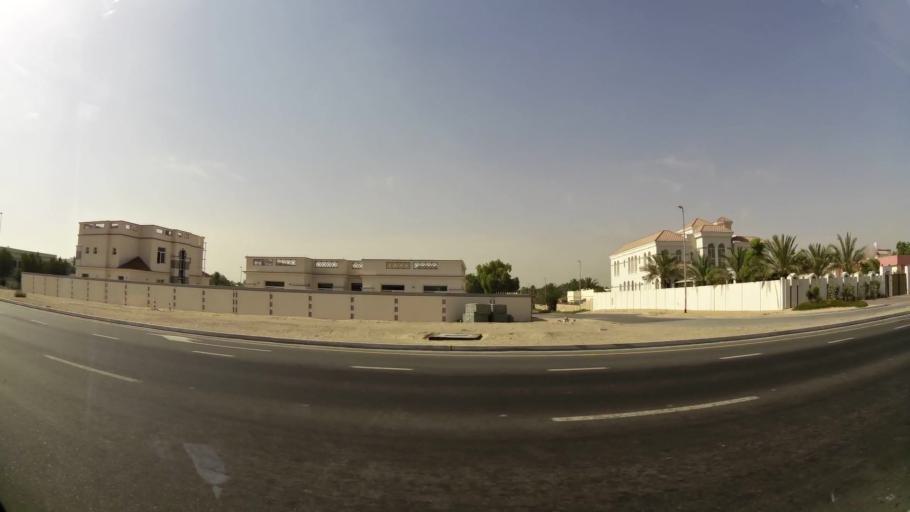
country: AE
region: Ash Shariqah
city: Sharjah
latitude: 25.2528
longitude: 55.4146
